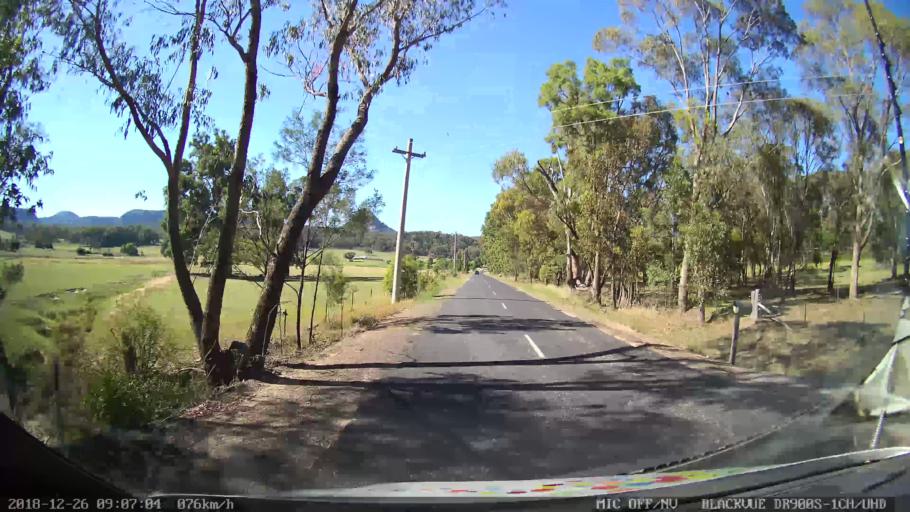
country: AU
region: New South Wales
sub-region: Mid-Western Regional
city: Kandos
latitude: -32.7014
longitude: 150.0051
